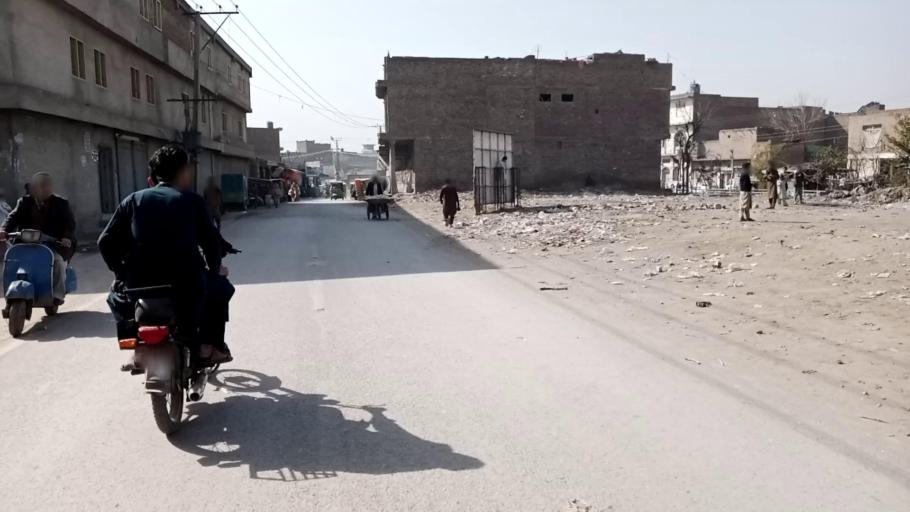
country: PK
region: Khyber Pakhtunkhwa
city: Peshawar
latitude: 33.9933
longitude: 71.5843
